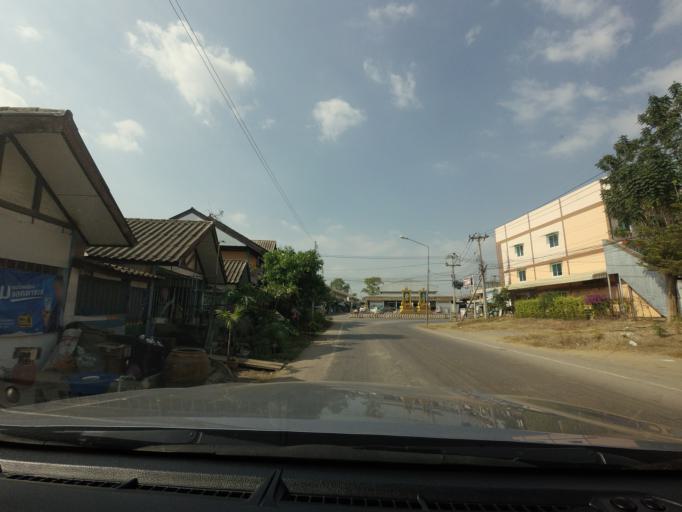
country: TH
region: Sukhothai
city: Kong Krailat
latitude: 16.9392
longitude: 99.9645
